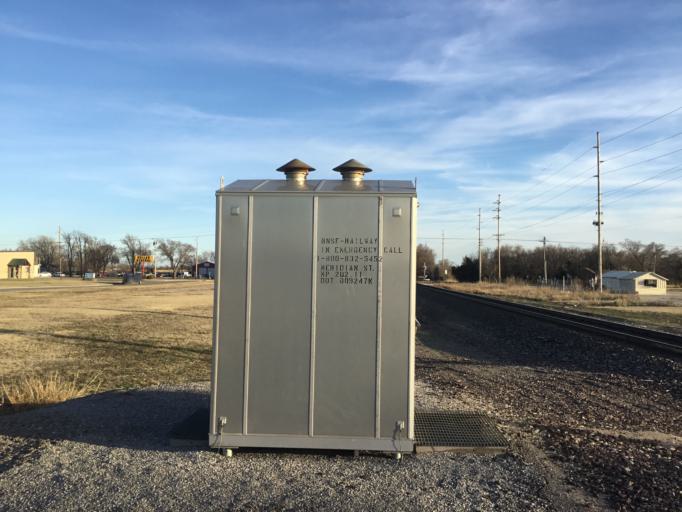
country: US
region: Kansas
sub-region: Sedgwick County
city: Valley Center
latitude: 37.8264
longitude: -97.3719
